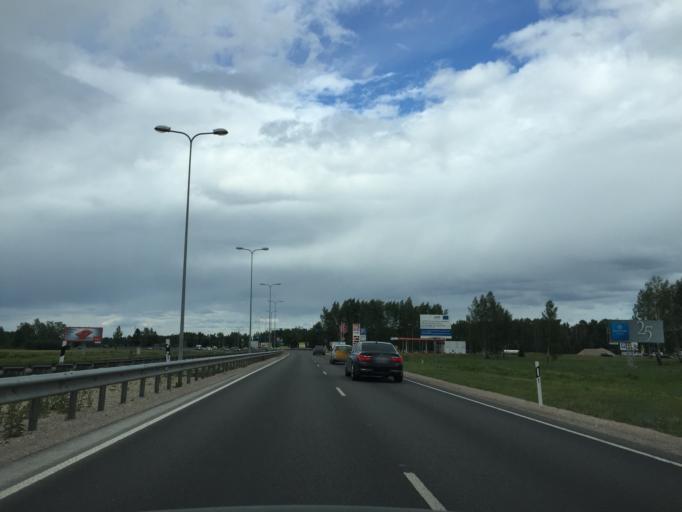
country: LV
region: Marupe
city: Marupe
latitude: 56.9220
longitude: 23.9885
